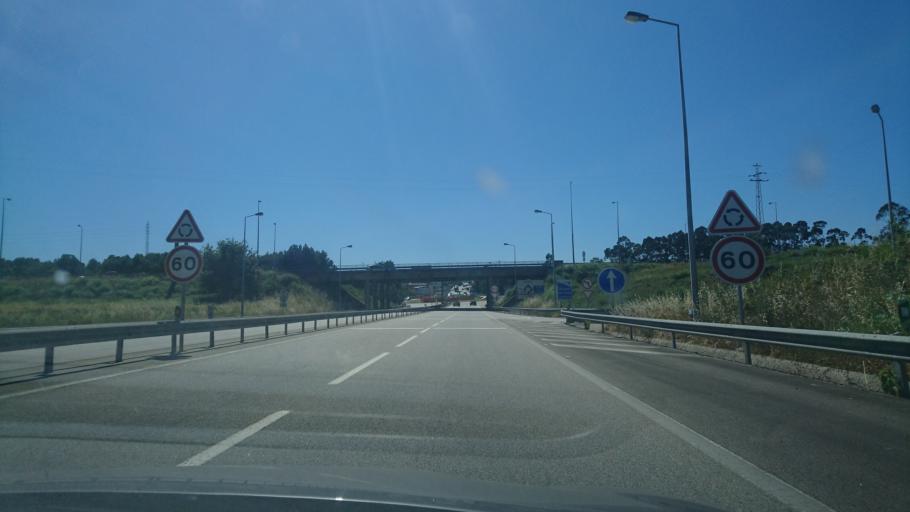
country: PT
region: Aveiro
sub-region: Espinho
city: Silvalde
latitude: 41.0085
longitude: -8.6183
